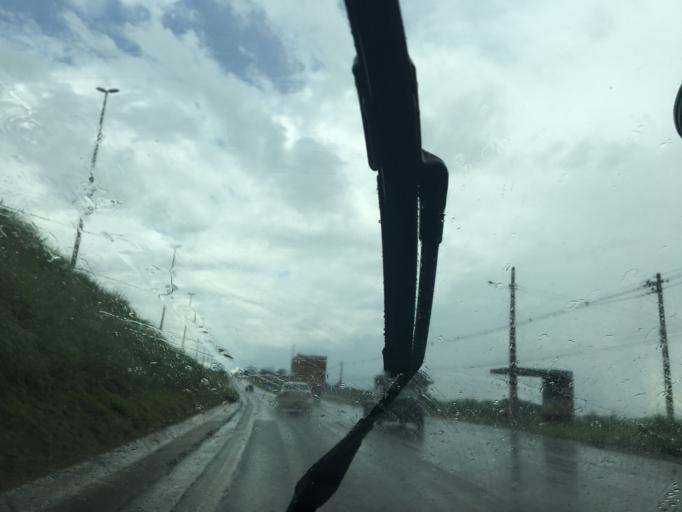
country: BR
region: Goias
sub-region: Luziania
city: Luziania
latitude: -16.1879
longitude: -47.9282
